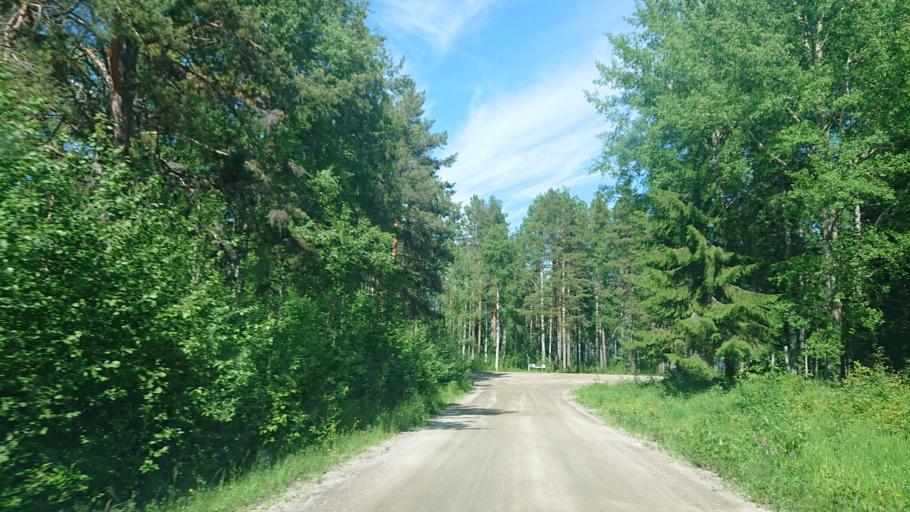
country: SE
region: Vaesternorrland
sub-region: Solleftea Kommun
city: Solleftea
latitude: 62.9701
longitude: 17.1600
